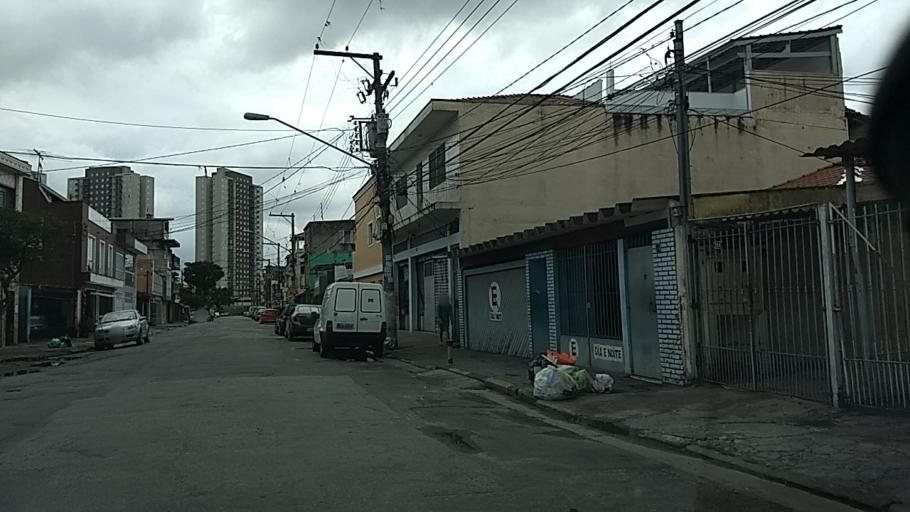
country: BR
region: Sao Paulo
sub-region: Guarulhos
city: Guarulhos
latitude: -23.4864
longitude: -46.5678
